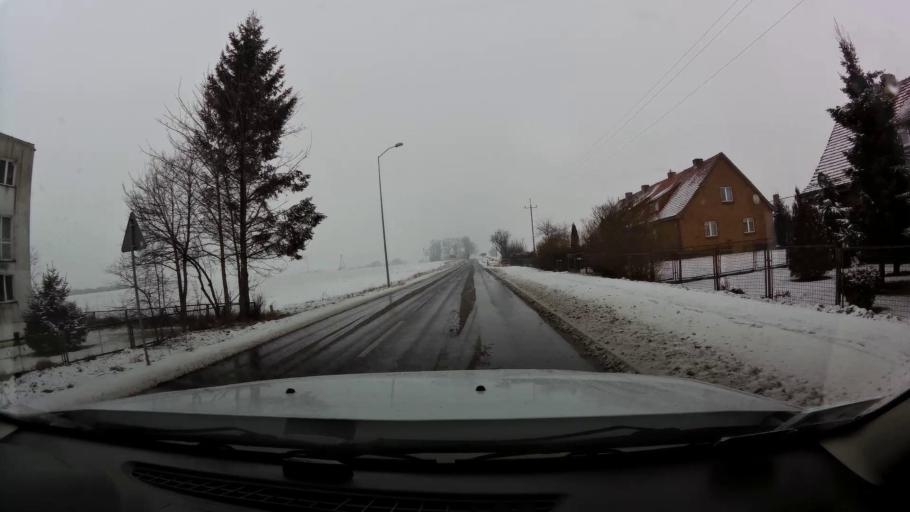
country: PL
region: West Pomeranian Voivodeship
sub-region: Powiat gryficki
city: Trzebiatow
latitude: 54.0783
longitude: 15.2569
